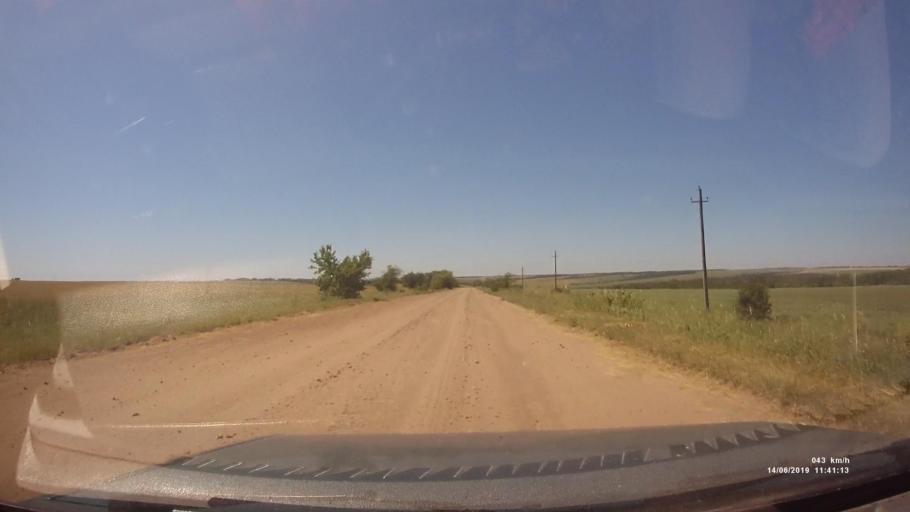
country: RU
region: Rostov
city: Kazanskaya
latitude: 49.8647
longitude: 41.3551
